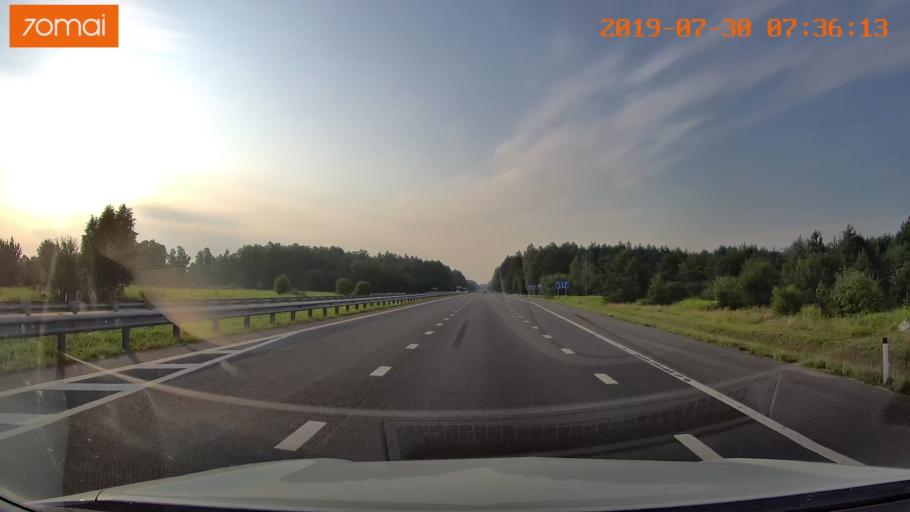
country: RU
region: Kaliningrad
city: Gvardeysk
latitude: 54.6665
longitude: 21.1194
